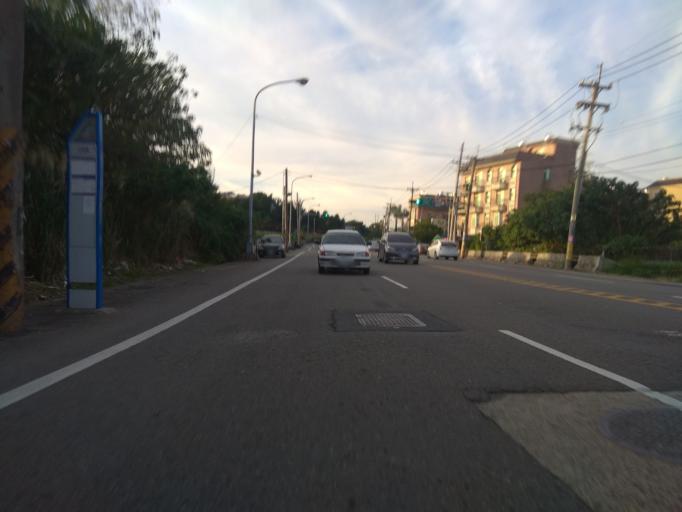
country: TW
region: Taiwan
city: Taoyuan City
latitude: 24.9761
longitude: 121.1961
